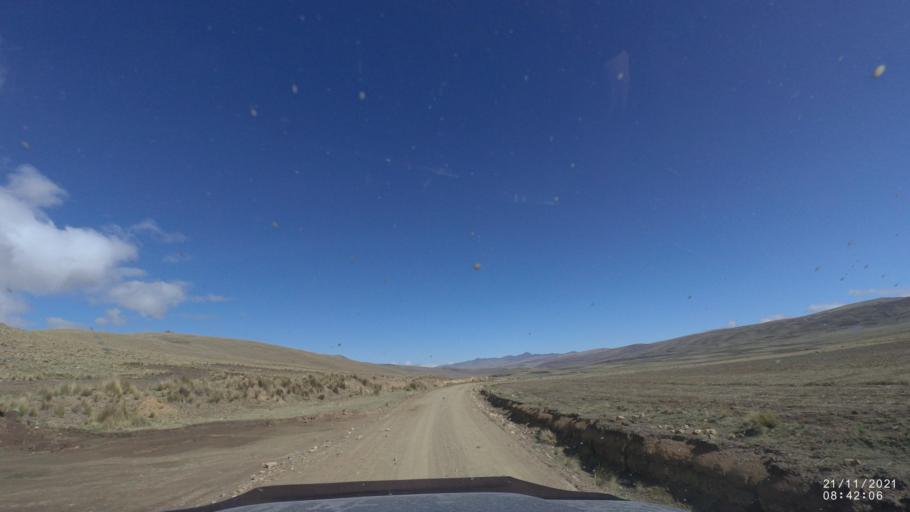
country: BO
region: Cochabamba
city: Cochabamba
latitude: -17.2679
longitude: -66.2203
